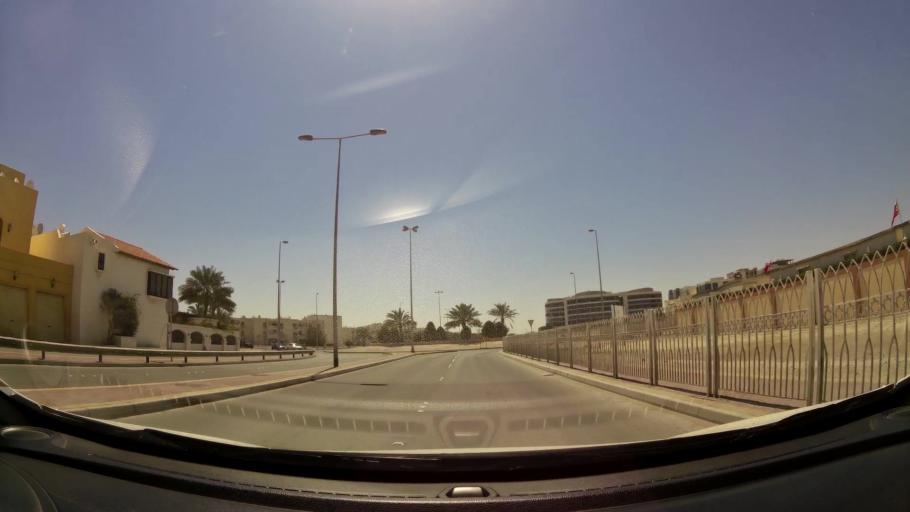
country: BH
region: Muharraq
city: Al Muharraq
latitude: 26.2675
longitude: 50.6031
